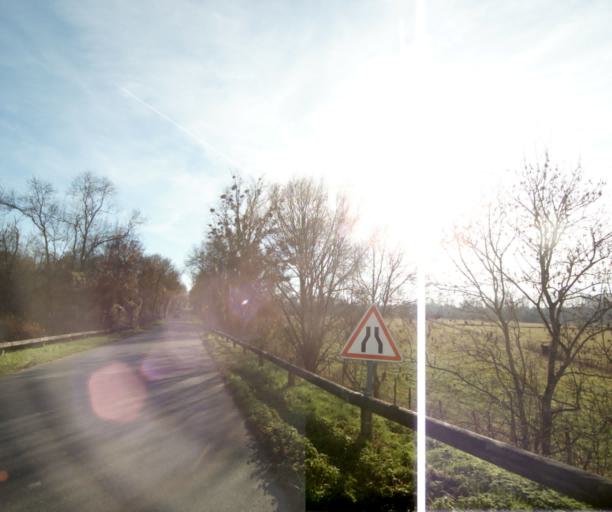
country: FR
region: Poitou-Charentes
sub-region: Departement de la Charente-Maritime
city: Chaniers
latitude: 45.7057
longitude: -0.5296
